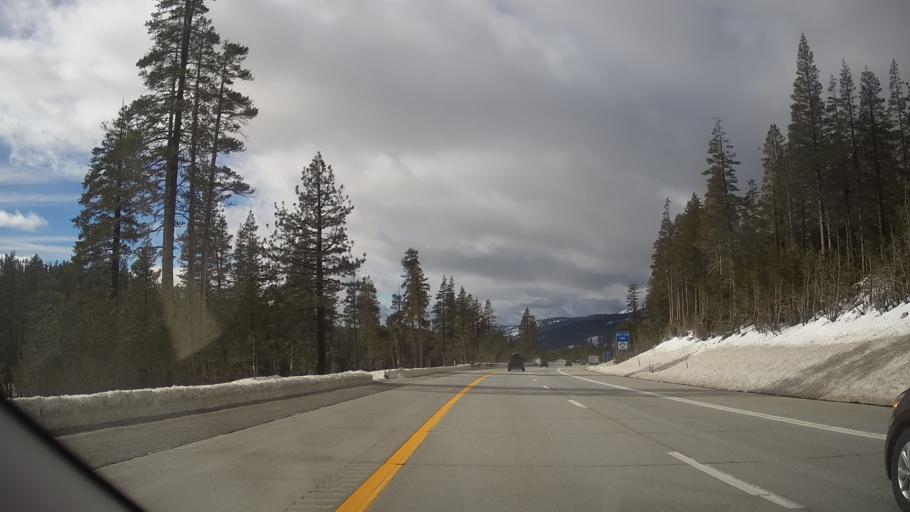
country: US
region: California
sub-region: Nevada County
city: Truckee
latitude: 39.3267
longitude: -120.3758
